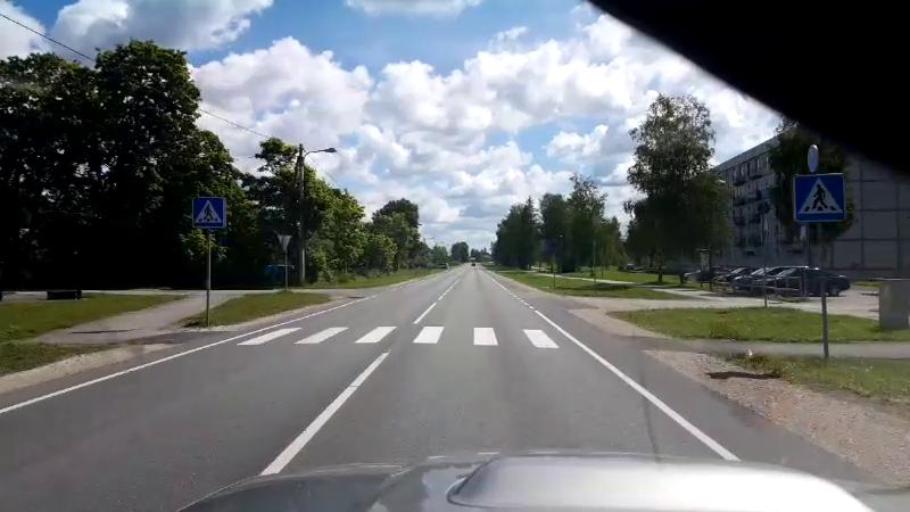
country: EE
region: Laeaene-Virumaa
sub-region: Tapa vald
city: Tapa
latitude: 59.2575
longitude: 25.9495
